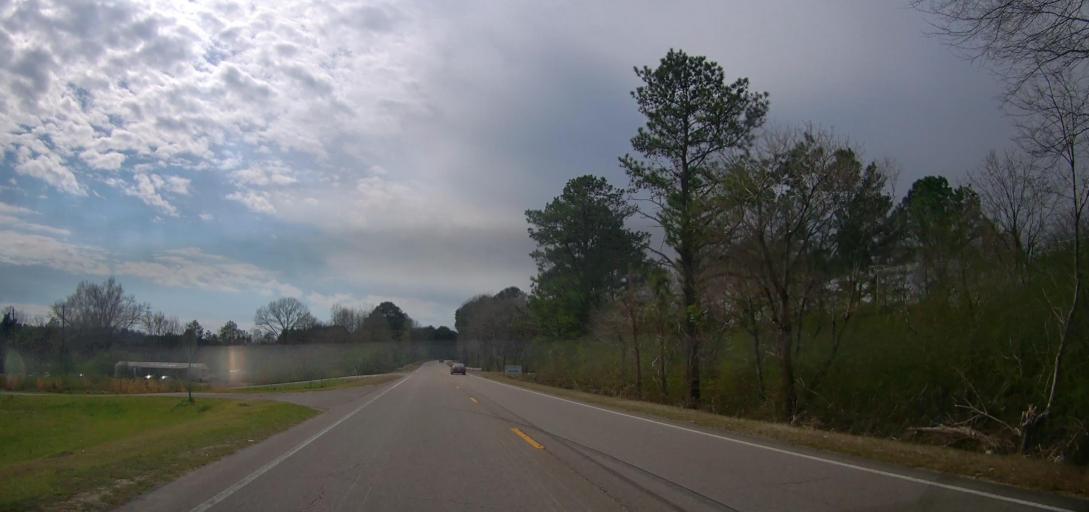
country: US
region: Alabama
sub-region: Walker County
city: Carbon Hill
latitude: 33.8764
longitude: -87.4822
